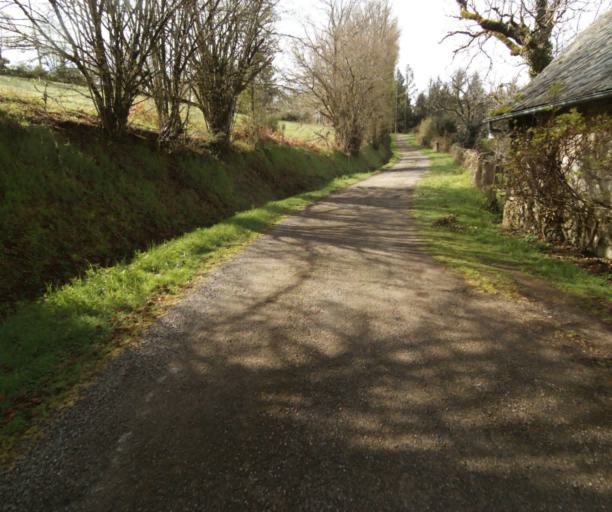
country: FR
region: Limousin
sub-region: Departement de la Correze
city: Tulle
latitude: 45.2856
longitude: 1.8207
